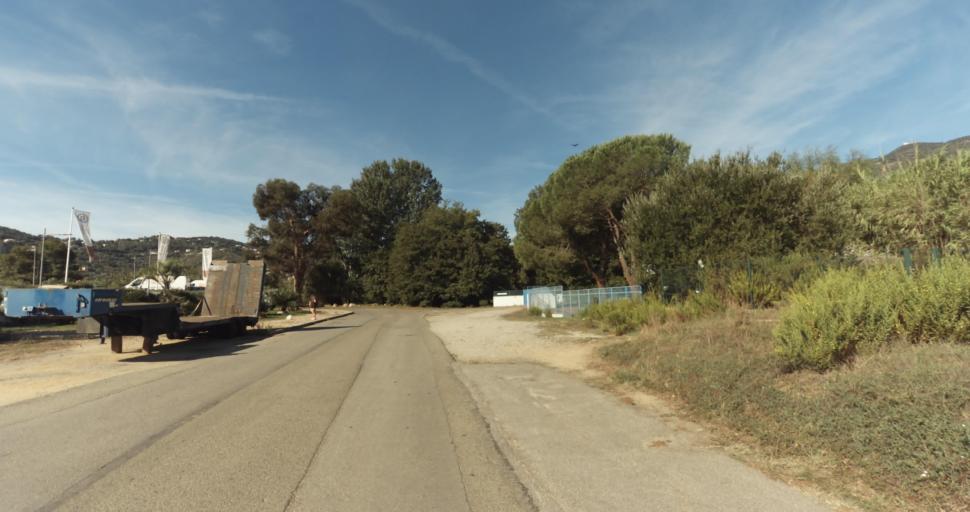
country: FR
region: Corsica
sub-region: Departement de la Corse-du-Sud
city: Ajaccio
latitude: 41.9363
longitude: 8.7338
